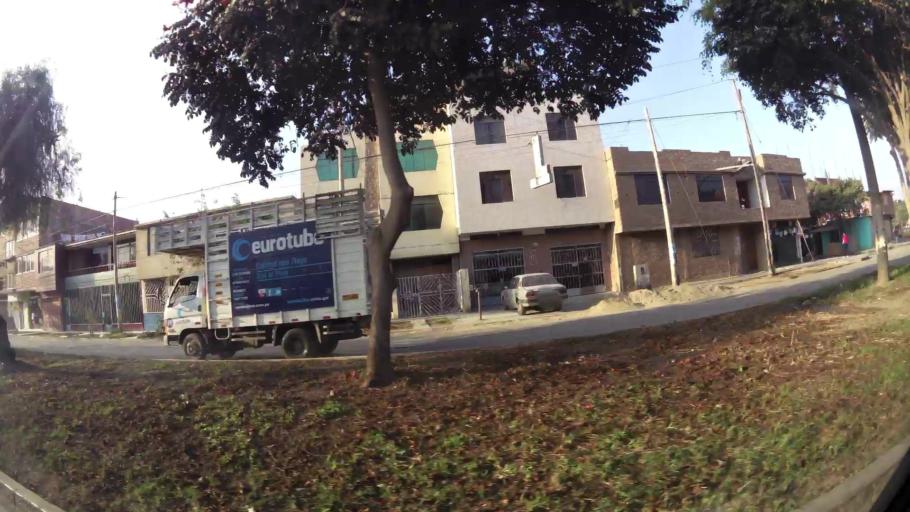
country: PE
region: La Libertad
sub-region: Provincia de Trujillo
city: El Porvenir
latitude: -8.0938
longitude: -78.9983
